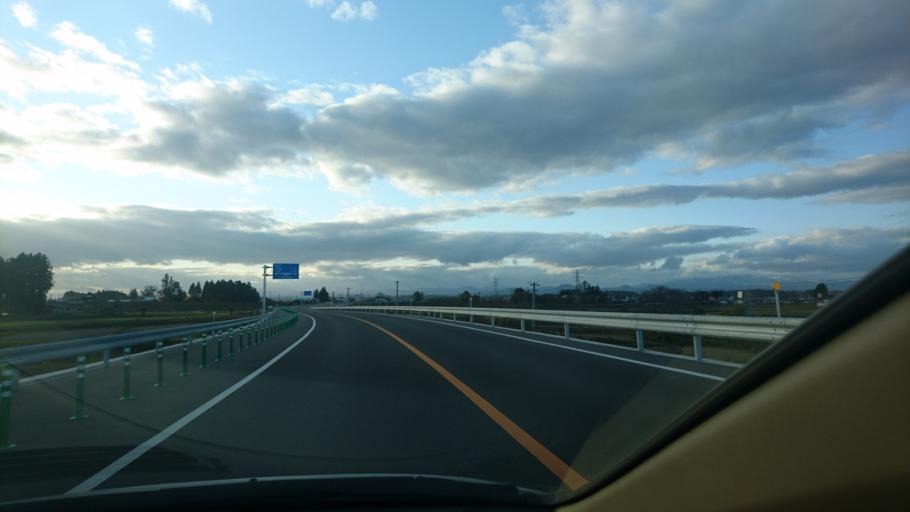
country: JP
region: Miyagi
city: Furukawa
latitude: 38.7383
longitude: 141.0427
